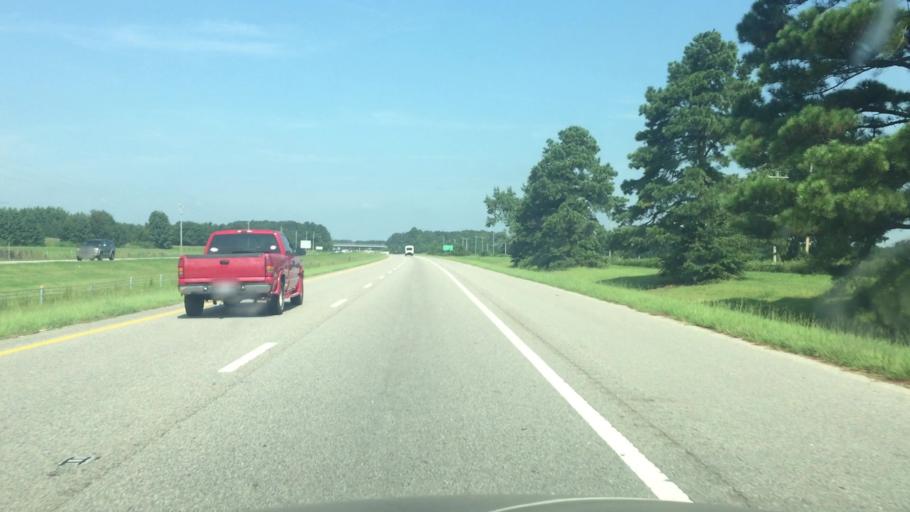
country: US
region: North Carolina
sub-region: Robeson County
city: Lumberton
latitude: 34.5861
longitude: -79.0586
